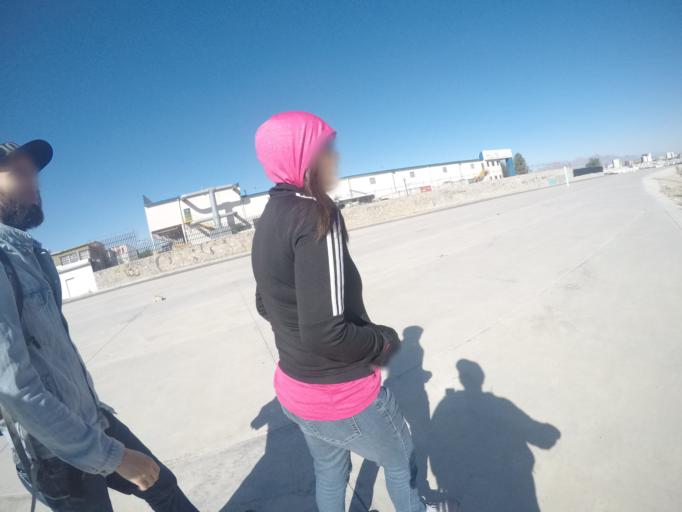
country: US
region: Texas
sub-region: El Paso County
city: Socorro
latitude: 31.6687
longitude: -106.4014
